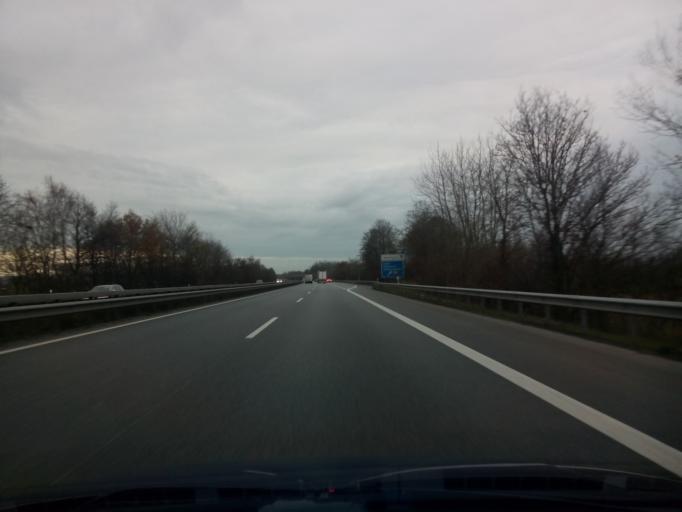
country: DE
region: Lower Saxony
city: Loxstedt
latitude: 53.4474
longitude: 8.5858
